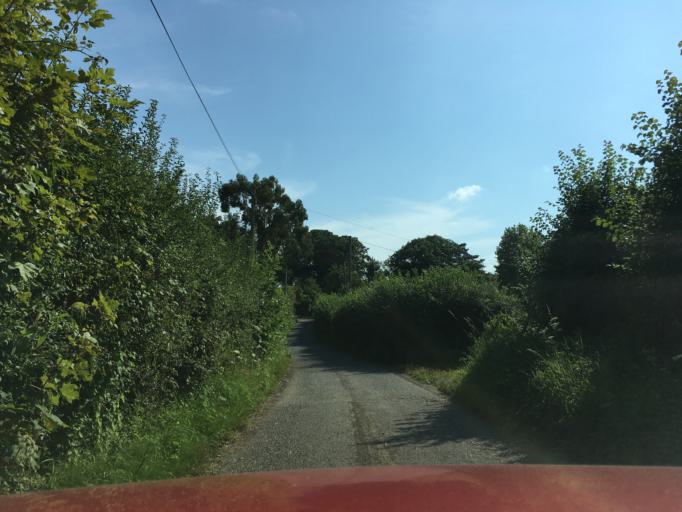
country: GB
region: England
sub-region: Gloucestershire
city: Dursley
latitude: 51.7042
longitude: -2.3150
